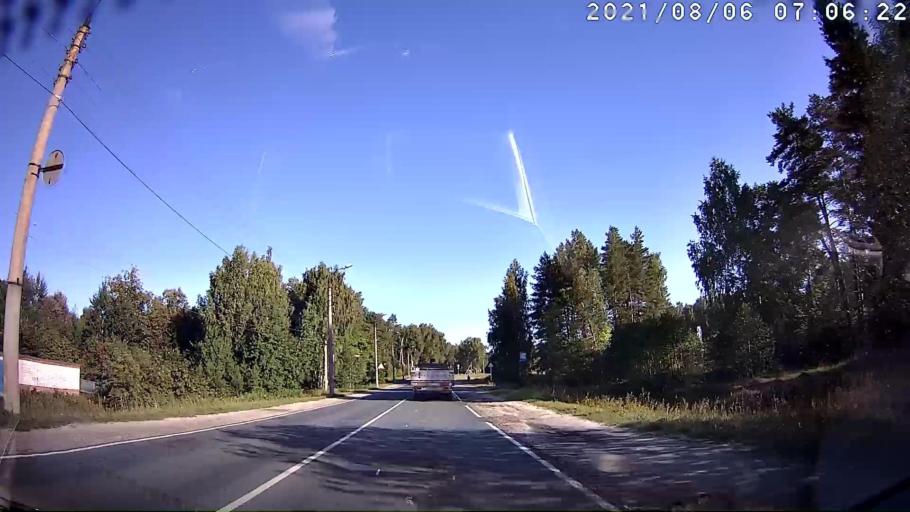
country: RU
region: Mariy-El
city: Yoshkar-Ola
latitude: 56.5585
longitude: 47.9815
